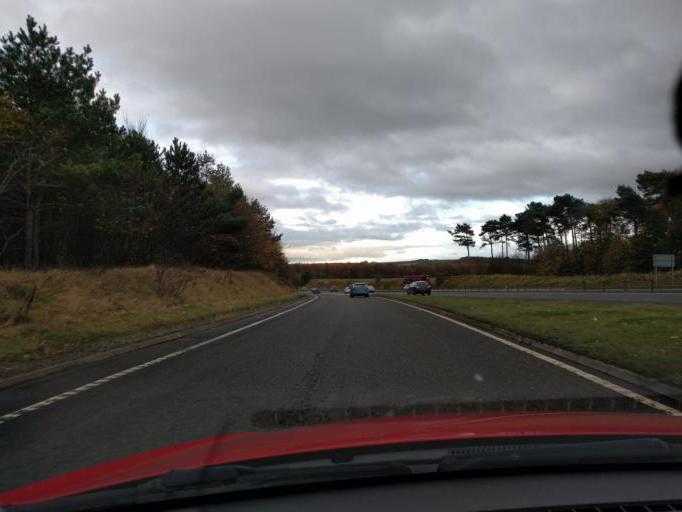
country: GB
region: Scotland
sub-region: East Lothian
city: Musselburgh
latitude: 55.9245
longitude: -3.0559
